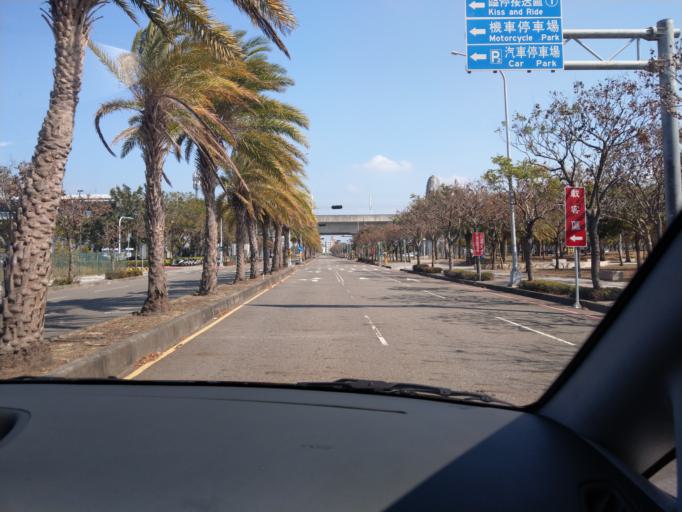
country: TW
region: Taiwan
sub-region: Chiayi
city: Taibao
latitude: 23.4572
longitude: 120.3218
